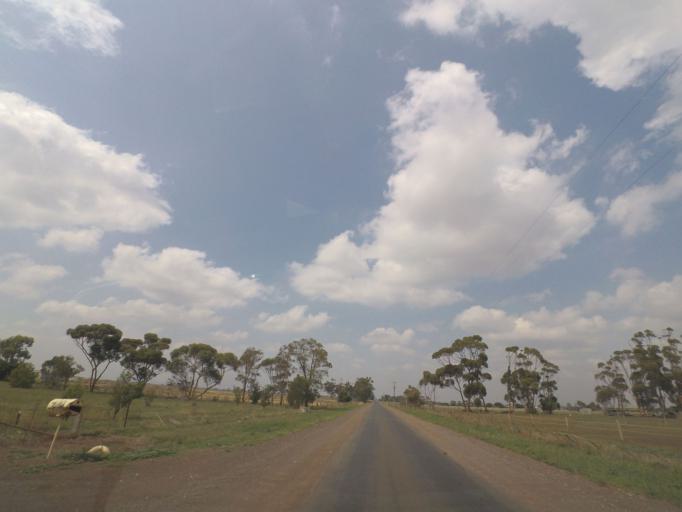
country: AU
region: Victoria
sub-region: Melton
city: Melton West
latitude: -37.6550
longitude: 144.5555
